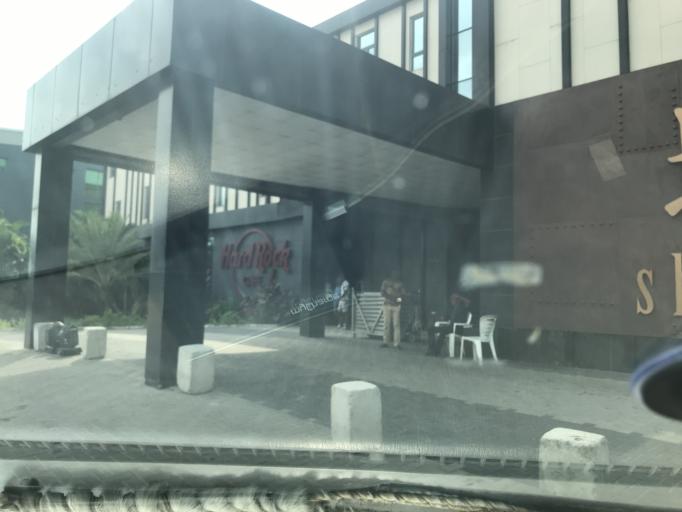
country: NG
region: Lagos
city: Ikoyi
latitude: 6.4232
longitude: 3.4443
